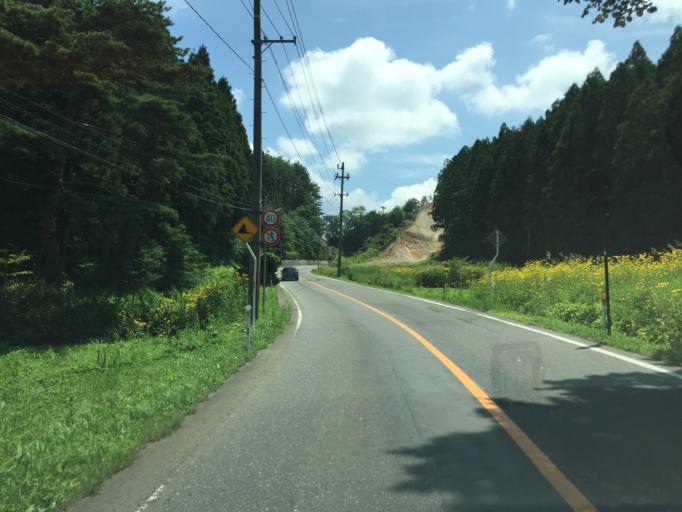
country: JP
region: Fukushima
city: Inawashiro
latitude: 37.3964
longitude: 140.0739
